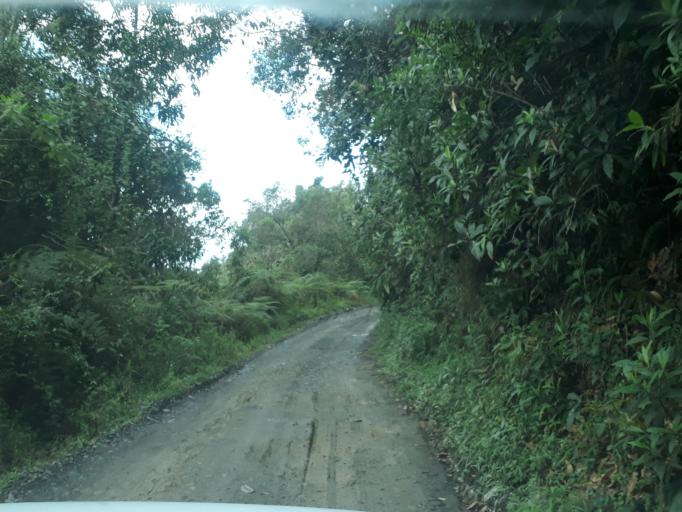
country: CO
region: Cundinamarca
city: Carmen de Carupa
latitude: 5.3537
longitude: -74.0651
